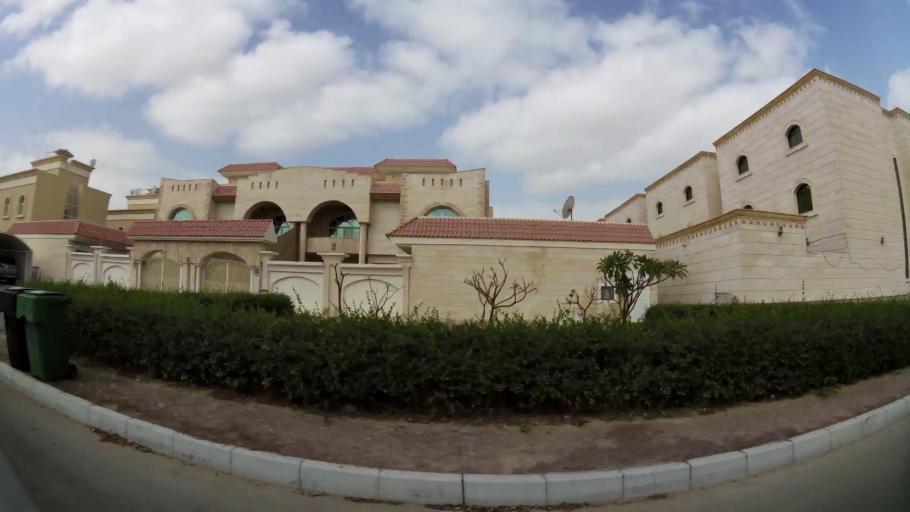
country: AE
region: Abu Dhabi
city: Abu Dhabi
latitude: 24.4128
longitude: 54.4973
